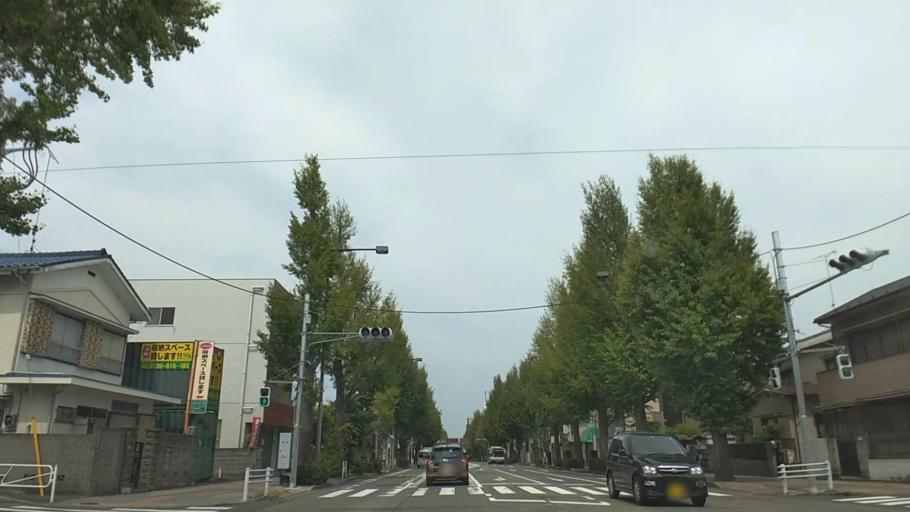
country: JP
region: Tokyo
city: Hachioji
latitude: 35.6554
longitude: 139.3074
